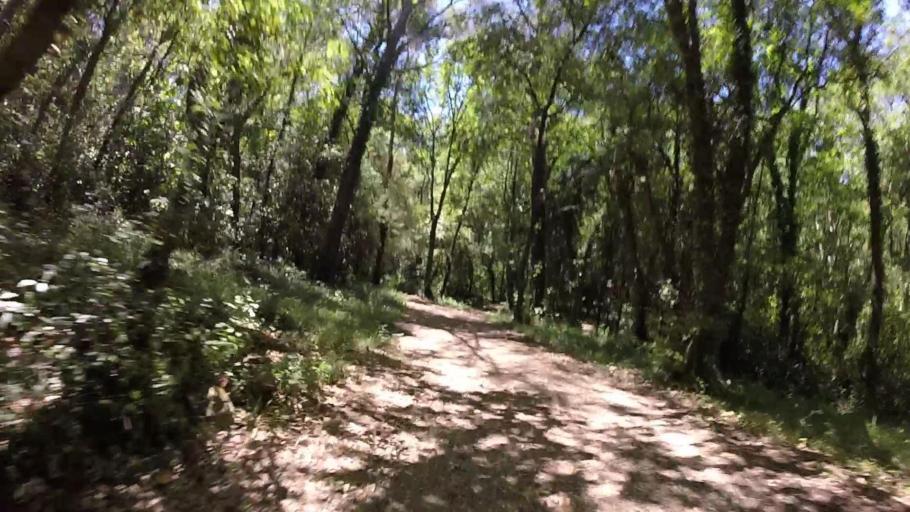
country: FR
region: Provence-Alpes-Cote d'Azur
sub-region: Departement des Alpes-Maritimes
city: Valbonne
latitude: 43.6305
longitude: 7.0157
